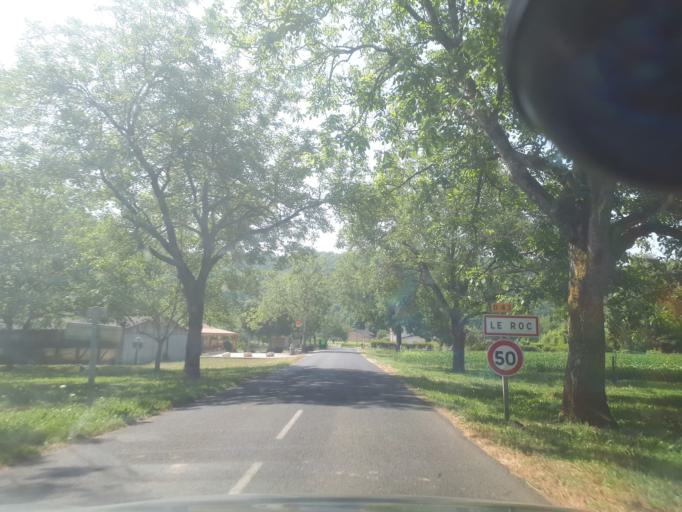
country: FR
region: Midi-Pyrenees
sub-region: Departement du Lot
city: Souillac
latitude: 44.8707
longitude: 1.4420
